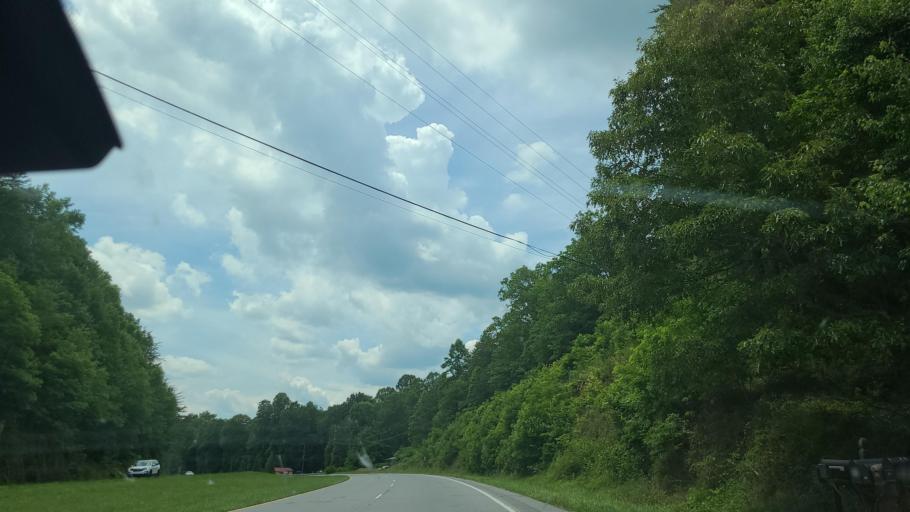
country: US
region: Georgia
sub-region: Fannin County
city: McCaysville
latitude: 35.0213
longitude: -84.2488
